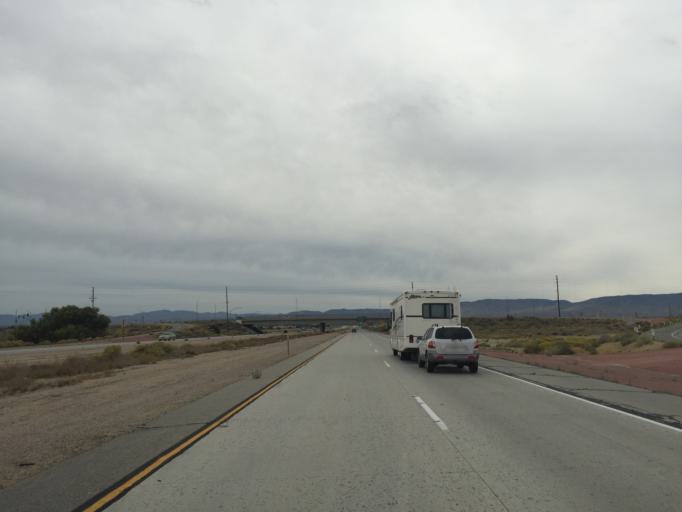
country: US
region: California
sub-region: Los Angeles County
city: Lancaster
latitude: 34.7214
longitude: -118.1704
